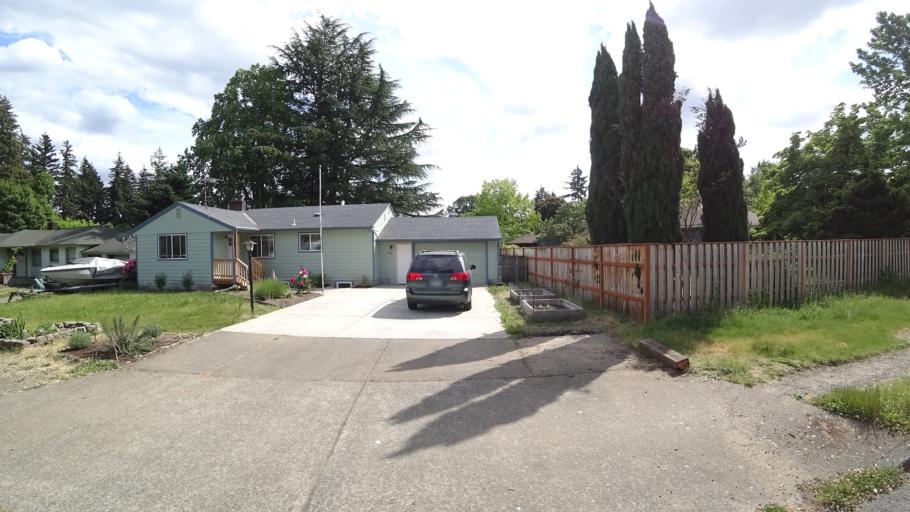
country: US
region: Oregon
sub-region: Multnomah County
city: Lents
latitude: 45.4949
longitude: -122.5452
